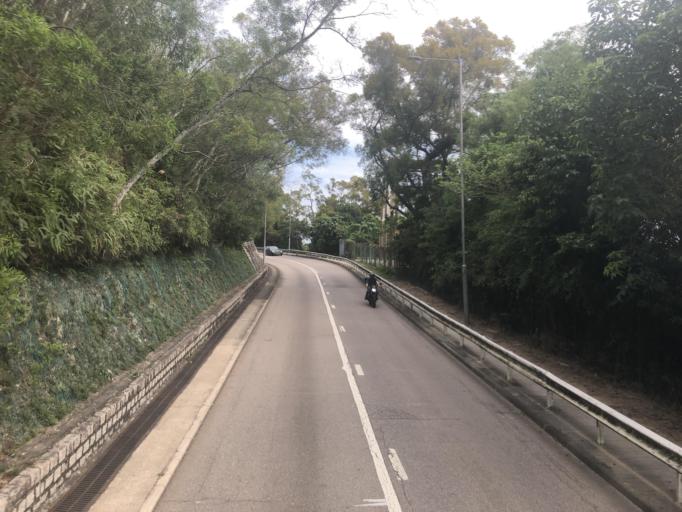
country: HK
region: Sai Kung
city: Sai Kung
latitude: 22.3875
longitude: 114.3032
